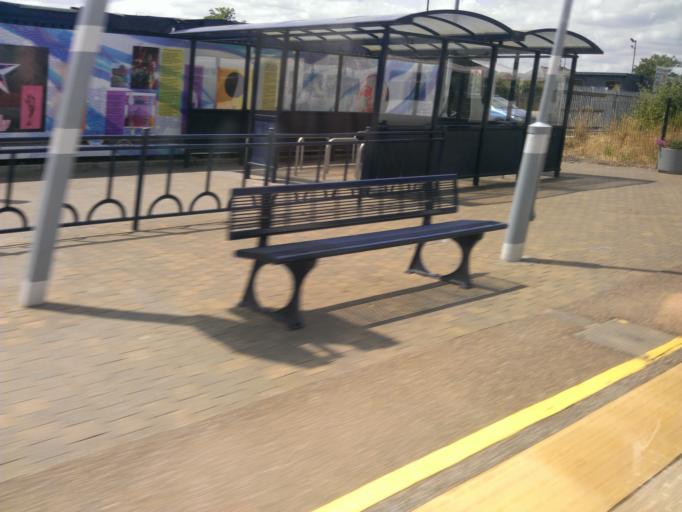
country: GB
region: England
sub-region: Essex
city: Colchester
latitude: 51.8856
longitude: 0.9277
